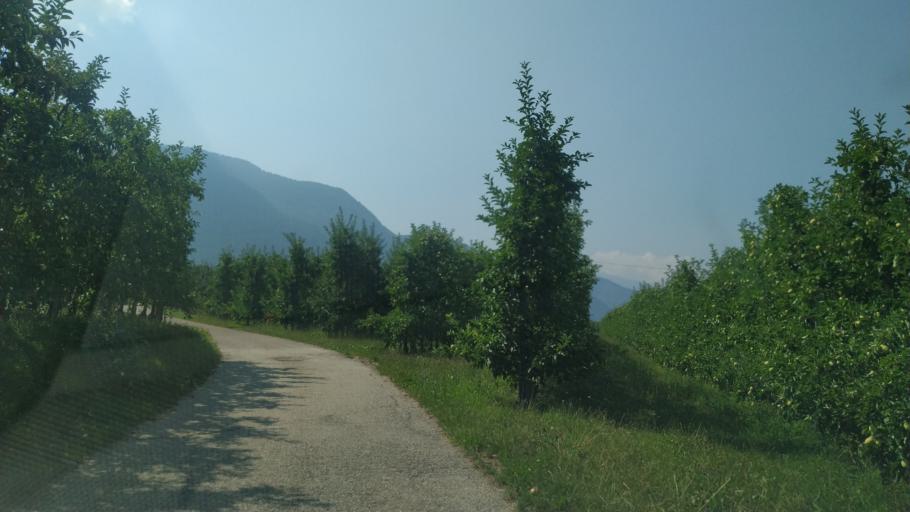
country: IT
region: Trentino-Alto Adige
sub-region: Provincia di Trento
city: Vigo di Ton
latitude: 46.2737
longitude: 11.0841
